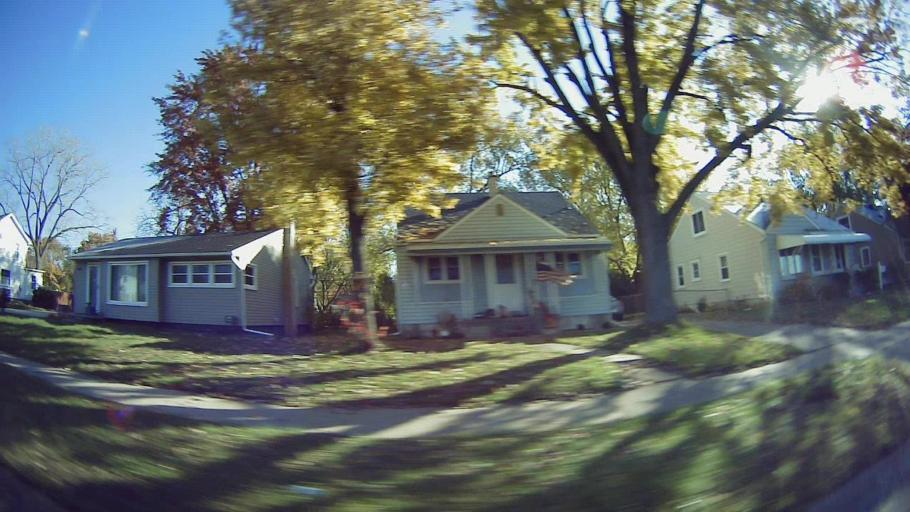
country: US
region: Michigan
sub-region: Oakland County
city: Lathrup Village
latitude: 42.4916
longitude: -83.2025
